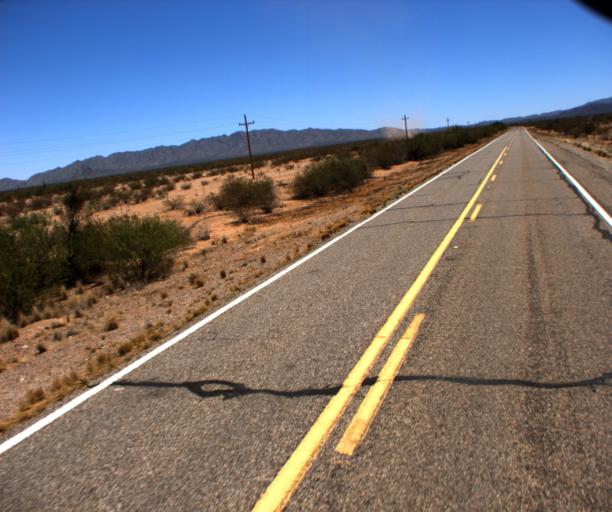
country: US
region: Arizona
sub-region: Pima County
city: Ajo
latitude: 32.1833
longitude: -112.3538
